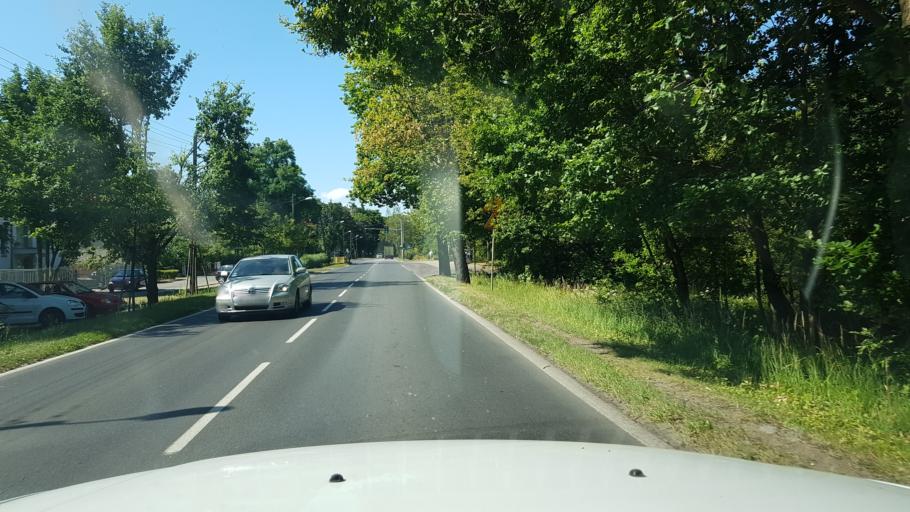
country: PL
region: West Pomeranian Voivodeship
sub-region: Szczecin
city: Szczecin
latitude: 53.4022
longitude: 14.6884
